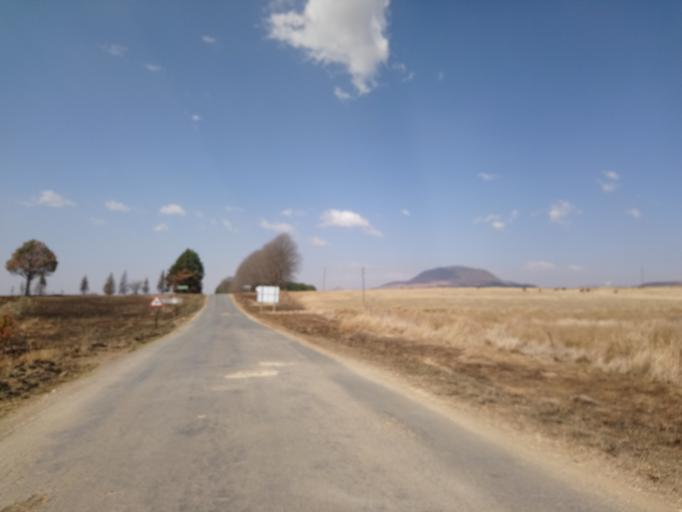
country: ZA
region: KwaZulu-Natal
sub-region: uMgungundlovu District Municipality
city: Mooirivier
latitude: -29.3223
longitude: 29.7230
